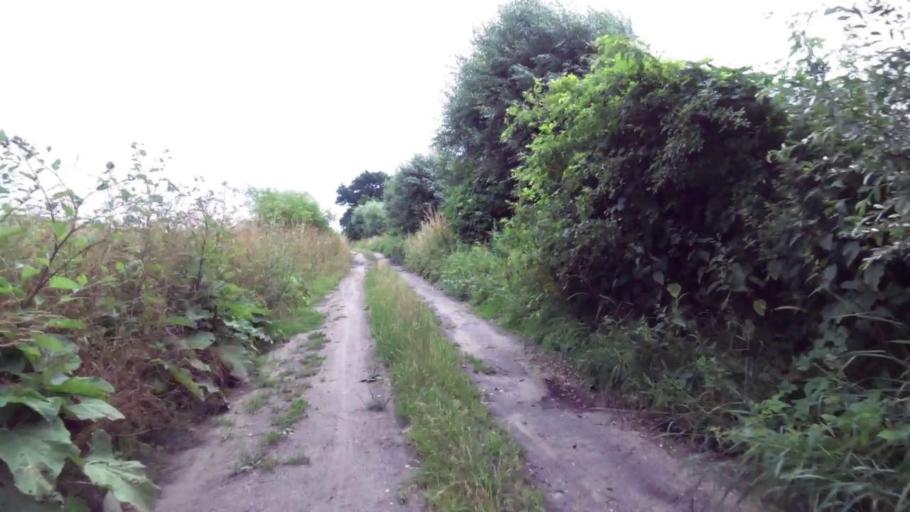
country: PL
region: West Pomeranian Voivodeship
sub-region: Powiat mysliborski
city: Mysliborz
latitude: 52.9636
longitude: 14.8987
